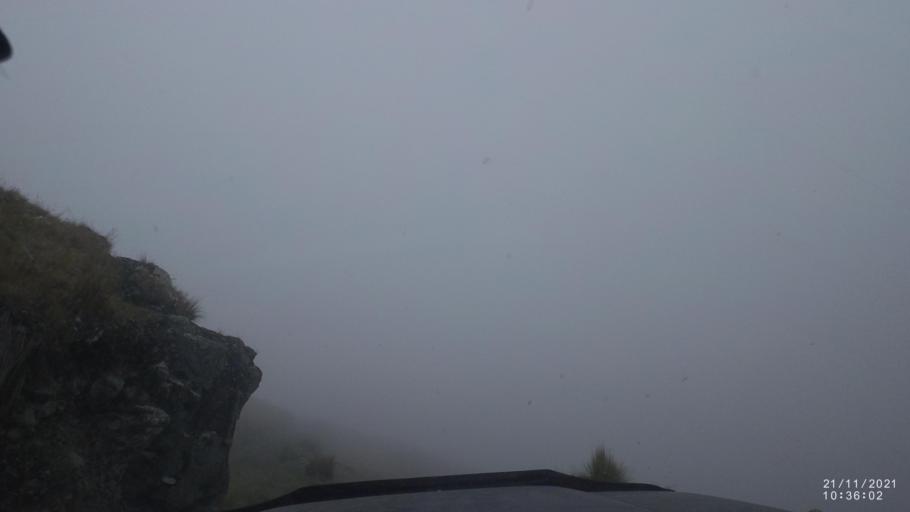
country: BO
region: Cochabamba
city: Cochabamba
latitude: -16.9721
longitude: -66.2673
